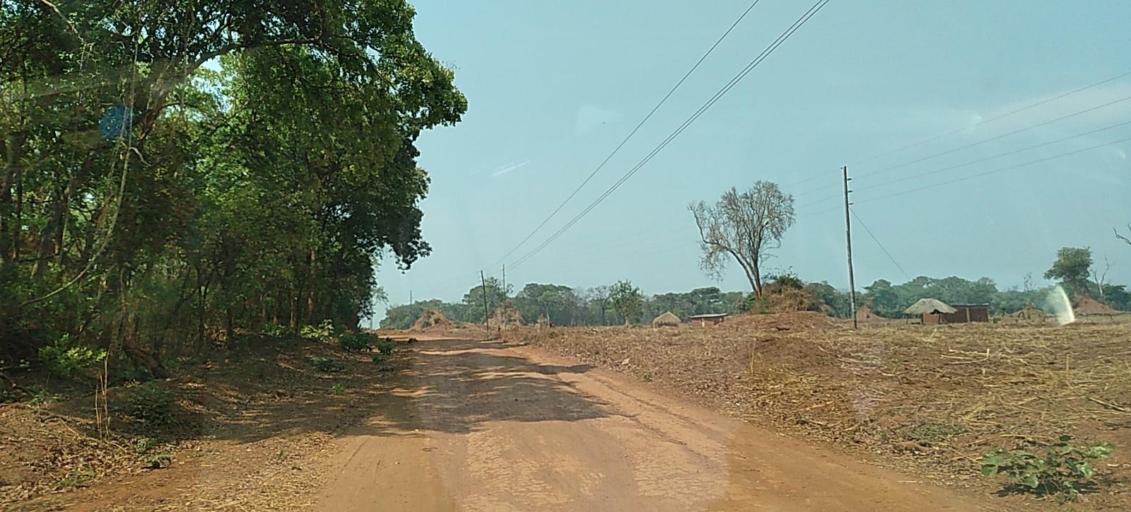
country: ZM
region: Copperbelt
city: Chingola
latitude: -13.0670
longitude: 27.4163
